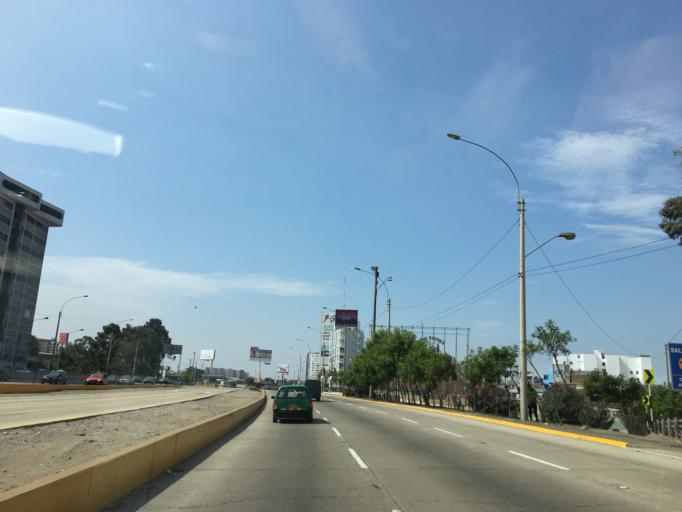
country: PE
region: Lima
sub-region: Lima
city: Surco
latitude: -12.1333
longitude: -77.0213
